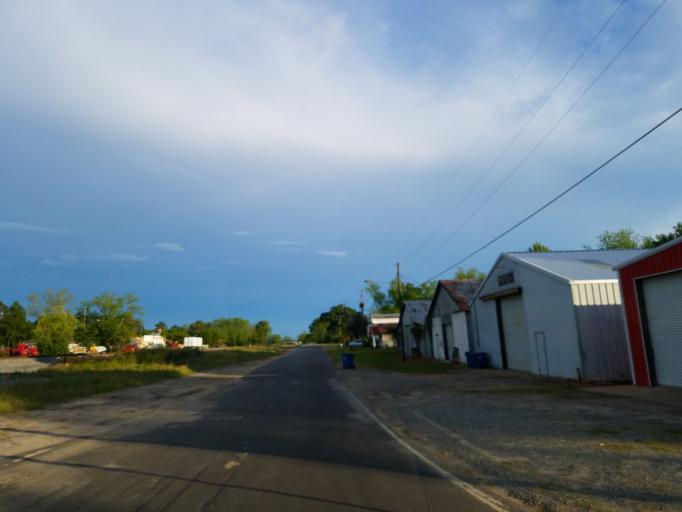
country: US
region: Georgia
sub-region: Turner County
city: Ashburn
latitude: 31.6707
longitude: -83.6362
